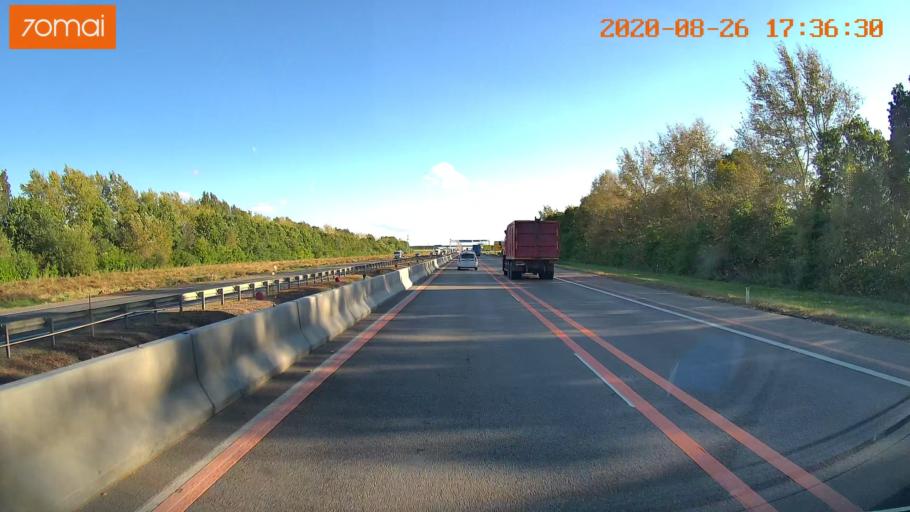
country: RU
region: Tula
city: Kazachka
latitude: 53.3708
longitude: 38.1833
